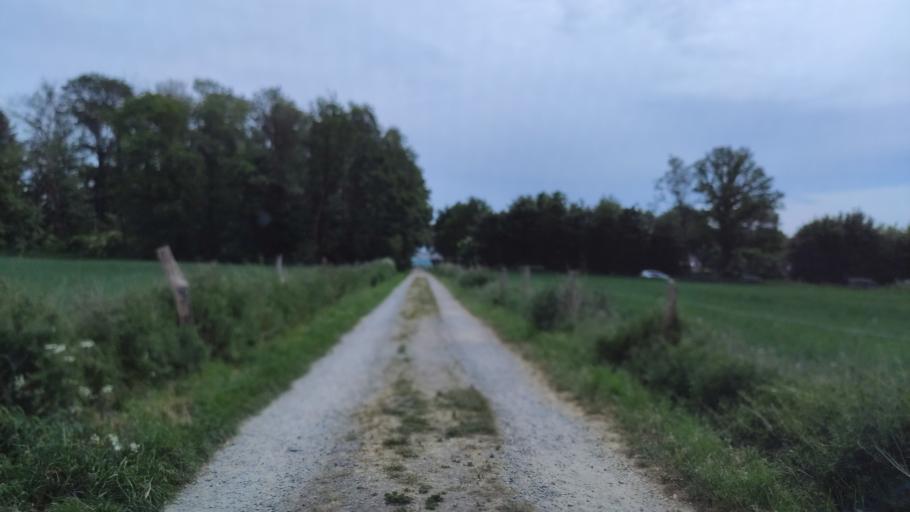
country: DE
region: North Rhine-Westphalia
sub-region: Regierungsbezirk Dusseldorf
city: Viersen
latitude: 51.2141
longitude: 6.4080
